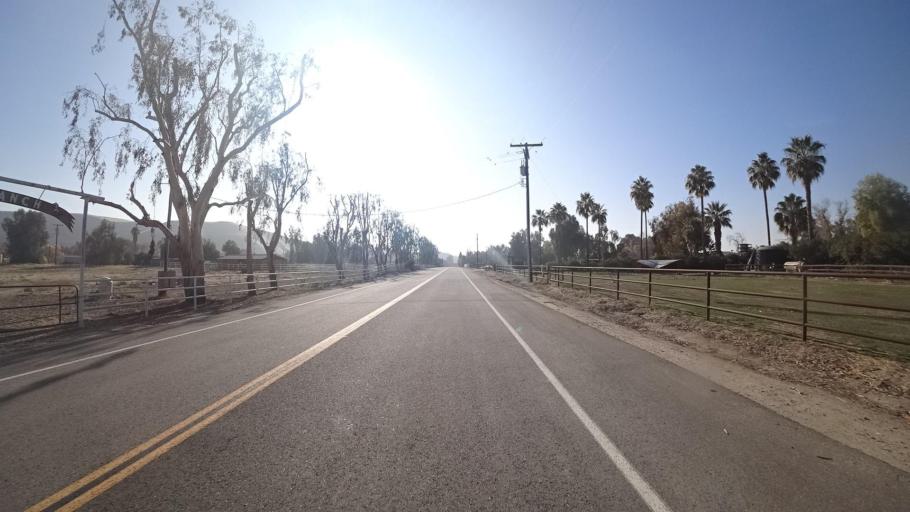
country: US
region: California
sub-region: Kern County
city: Oildale
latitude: 35.4536
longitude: -118.9100
